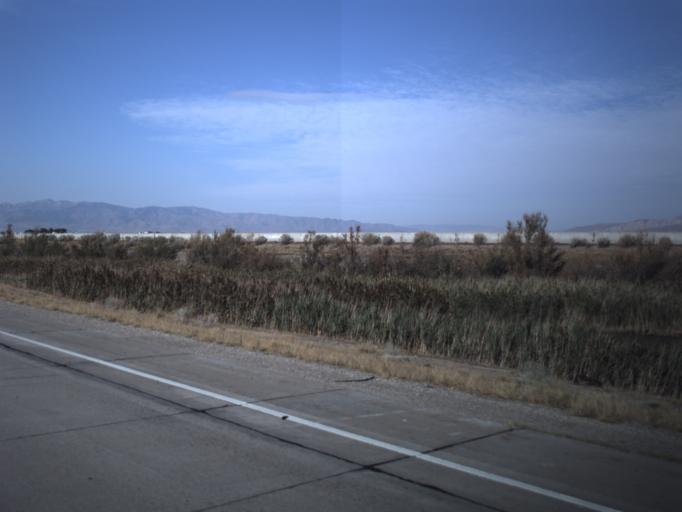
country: US
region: Utah
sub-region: Salt Lake County
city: Magna
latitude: 40.7405
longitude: -112.1895
